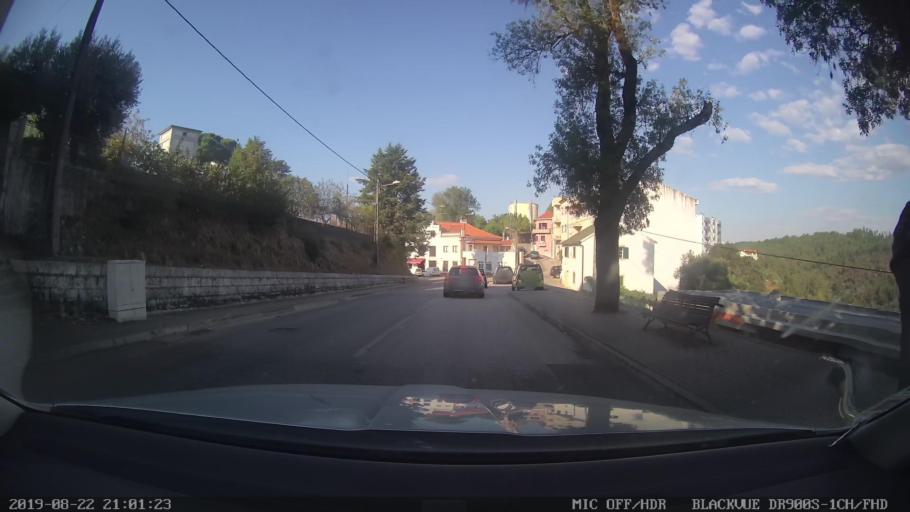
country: PT
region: Castelo Branco
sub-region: Serta
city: Serta
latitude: 39.8122
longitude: -8.0960
